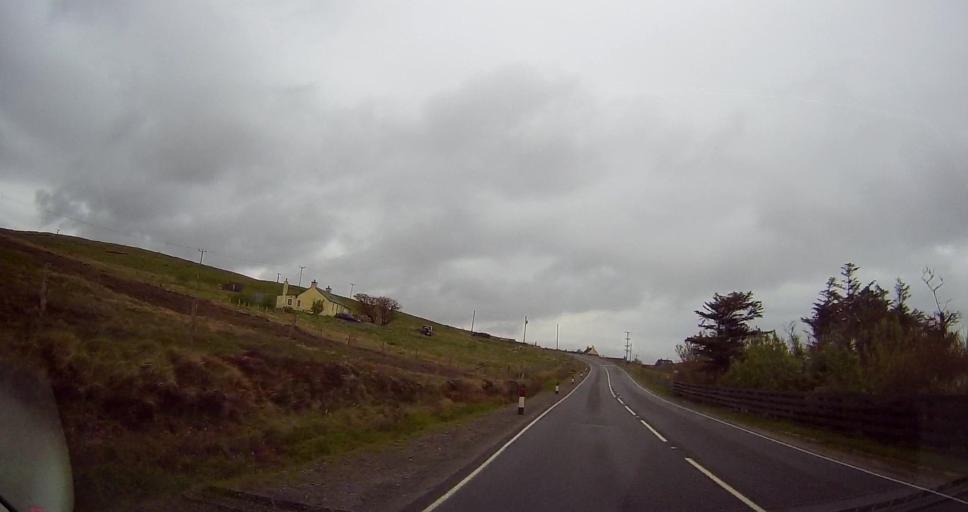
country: GB
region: Scotland
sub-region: Shetland Islands
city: Lerwick
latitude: 60.2359
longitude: -1.2324
